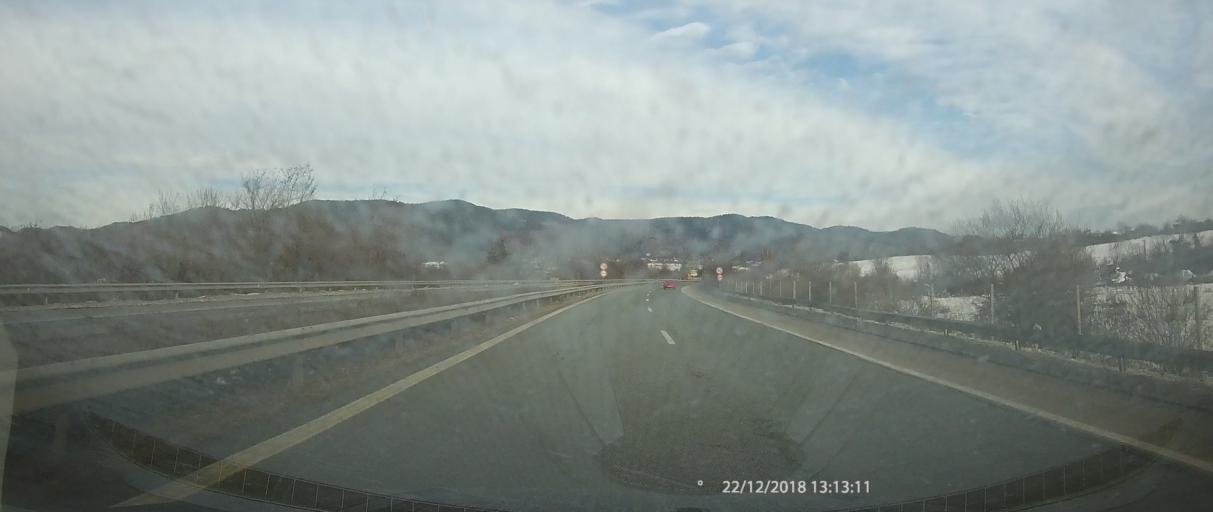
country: BG
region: Sofiya
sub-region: Obshtina Pravets
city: Pravets
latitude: 42.9030
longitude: 23.8618
